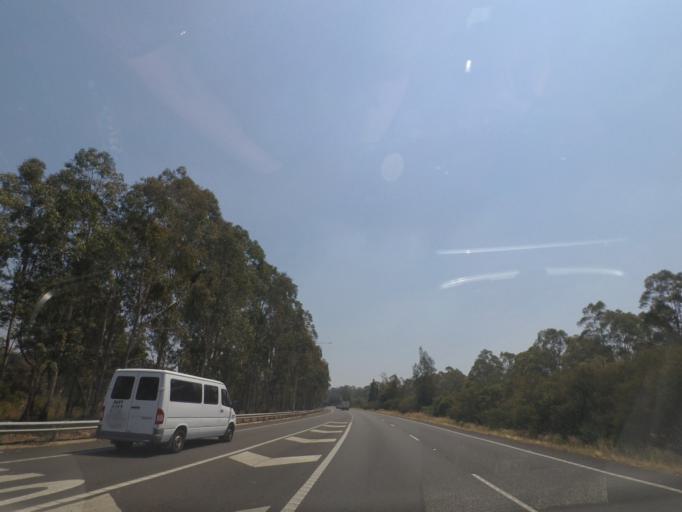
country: AU
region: New South Wales
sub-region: Newcastle
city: Beresfield
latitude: -32.8352
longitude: 151.6353
